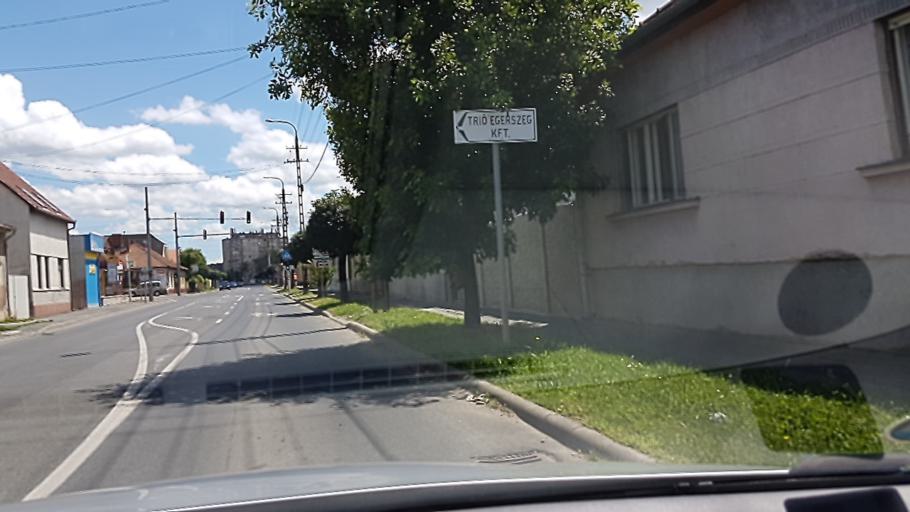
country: HU
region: Zala
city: Zalaegerszeg
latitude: 46.8493
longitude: 16.8222
